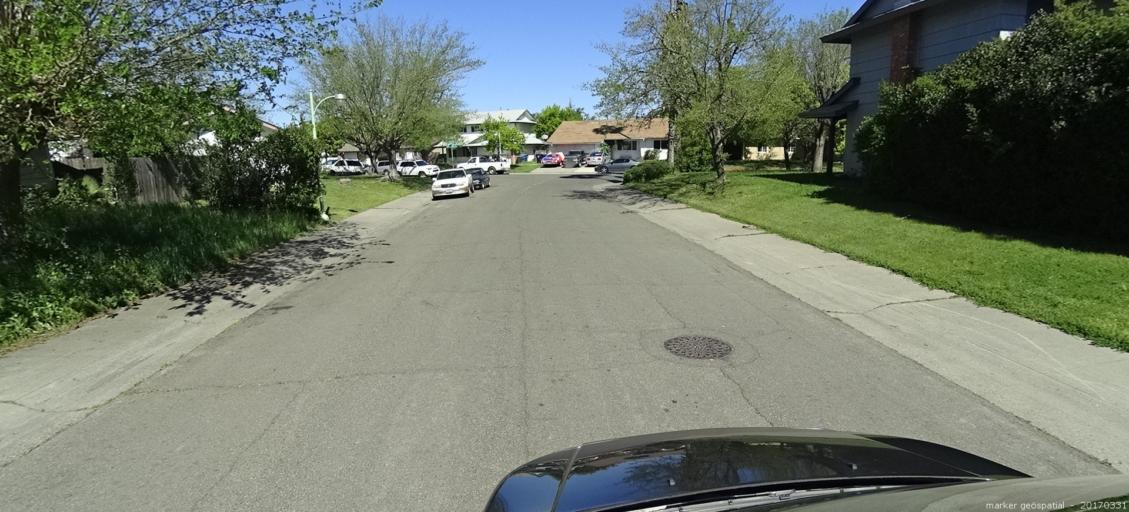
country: US
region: California
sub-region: Sacramento County
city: Florin
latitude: 38.4624
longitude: -121.4326
